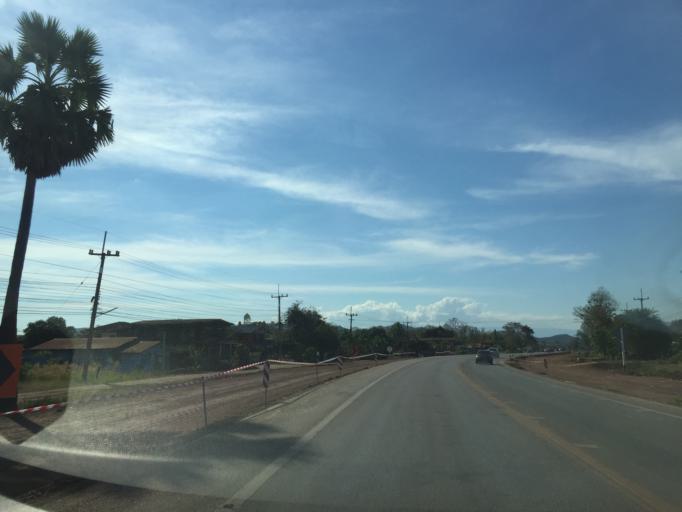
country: TH
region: Loei
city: Erawan
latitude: 17.2983
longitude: 101.8718
